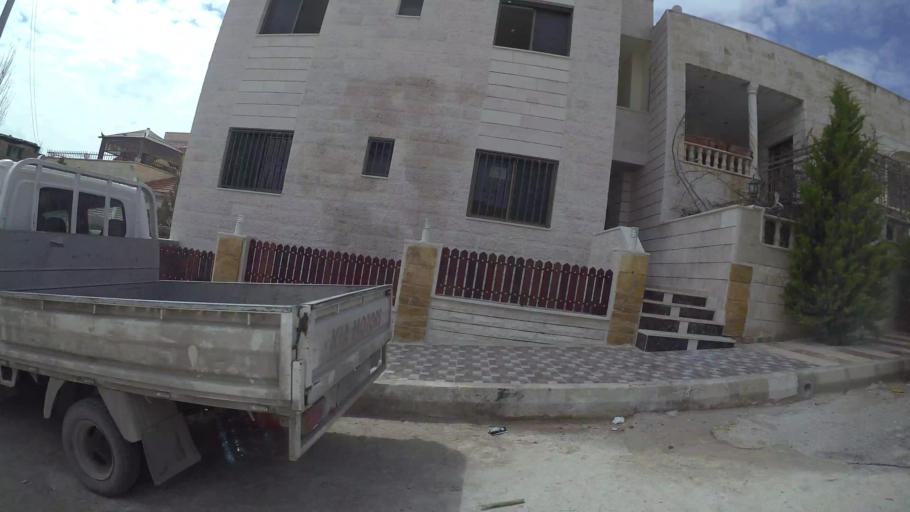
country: JO
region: Amman
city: Al Jubayhah
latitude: 32.0667
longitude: 35.8156
